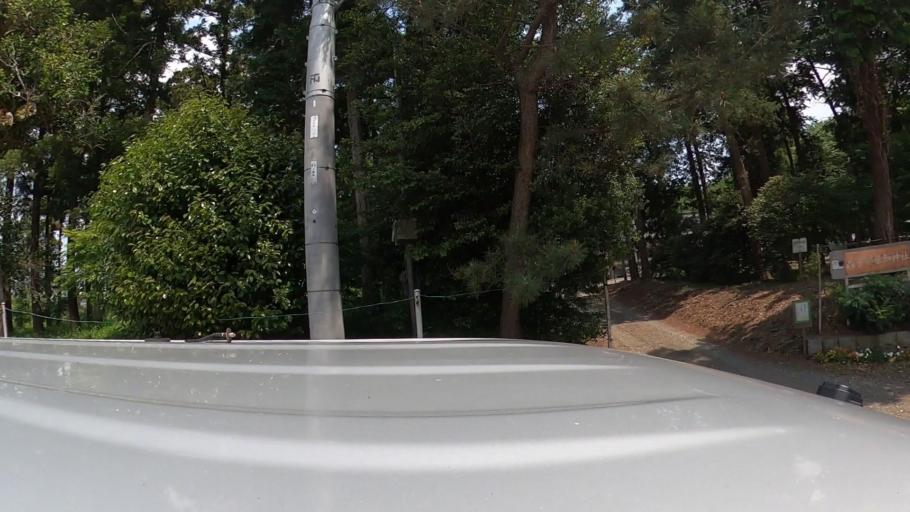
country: JP
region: Kanagawa
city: Chigasaki
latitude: 35.3920
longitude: 139.4208
